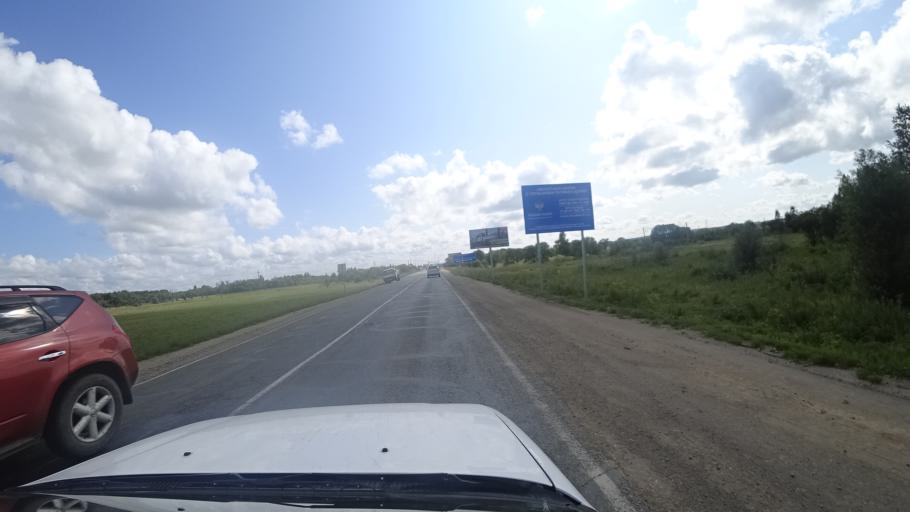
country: RU
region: Primorskiy
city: Dal'nerechensk
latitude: 45.9236
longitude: 133.7735
